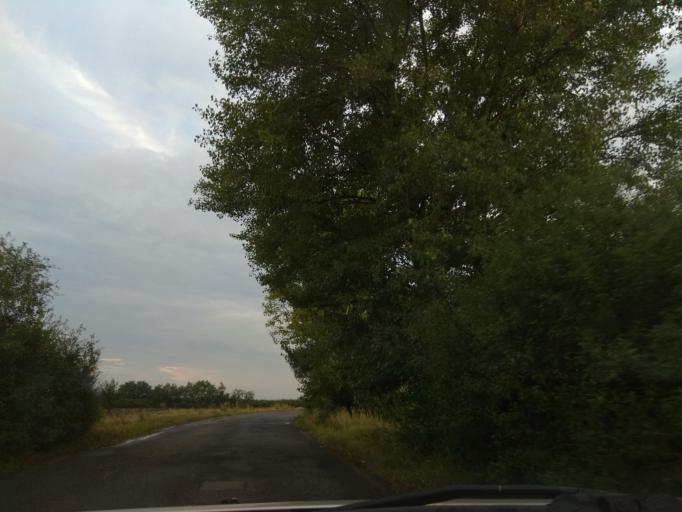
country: HU
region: Borsod-Abauj-Zemplen
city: Felsozsolca
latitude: 48.0813
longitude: 20.8455
